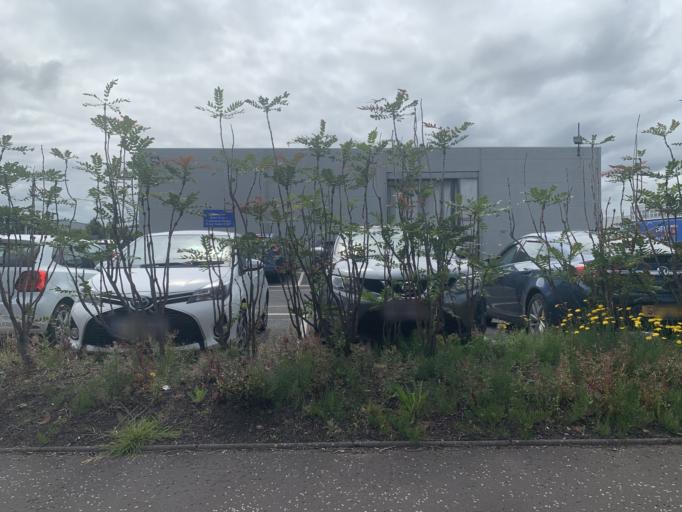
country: GB
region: Scotland
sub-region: Renfrewshire
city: Inchinnan
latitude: 55.8675
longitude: -4.4265
